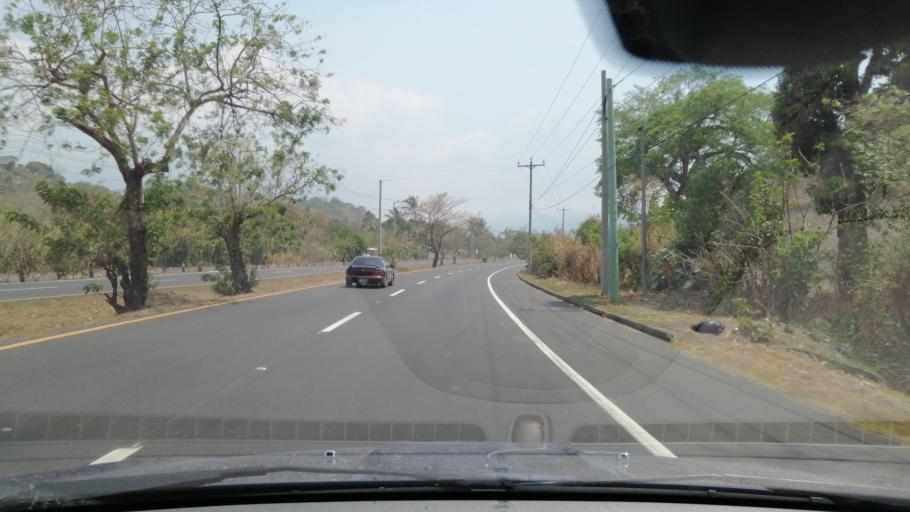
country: SV
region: La Libertad
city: Ciudad Arce
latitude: 13.8374
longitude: -89.4522
